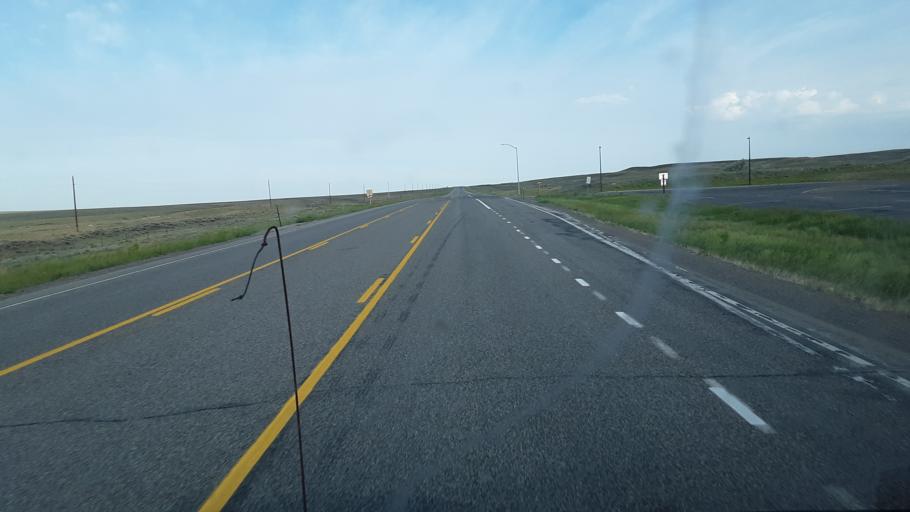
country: US
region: Wyoming
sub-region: Natrona County
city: Mills
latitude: 43.0744
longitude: -107.2445
